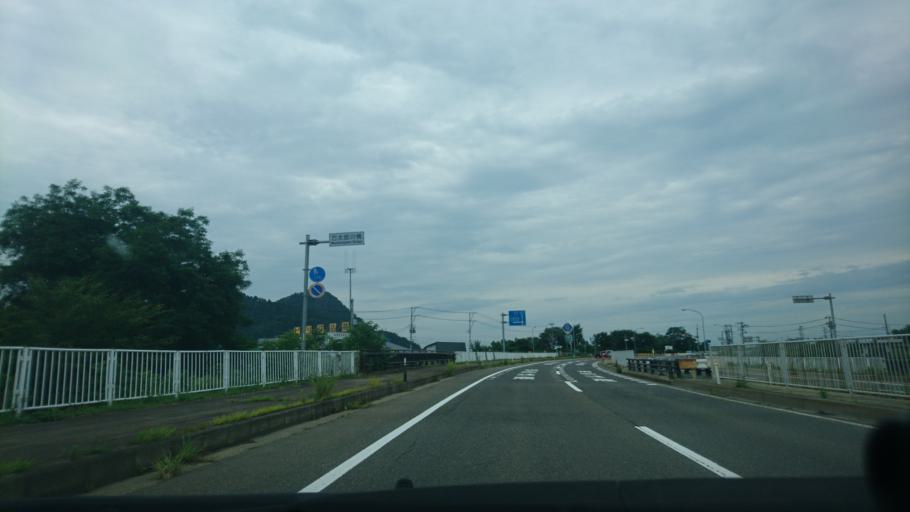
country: JP
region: Akita
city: Omagari
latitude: 39.4783
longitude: 140.4595
